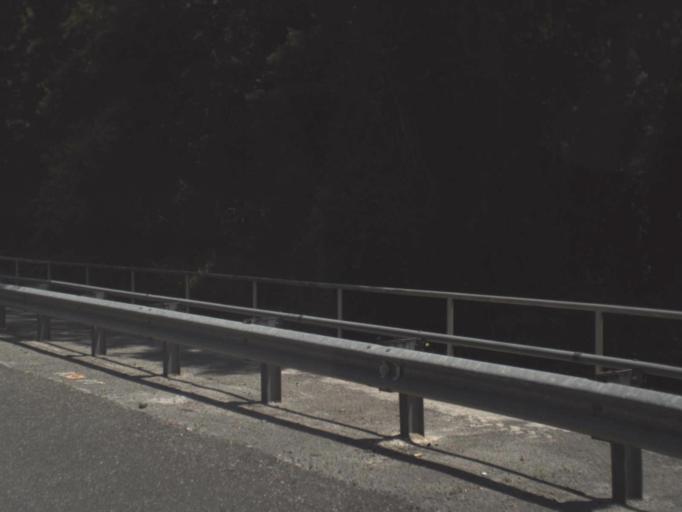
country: US
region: Florida
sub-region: Bradford County
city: Starke
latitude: 29.9385
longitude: -82.1062
